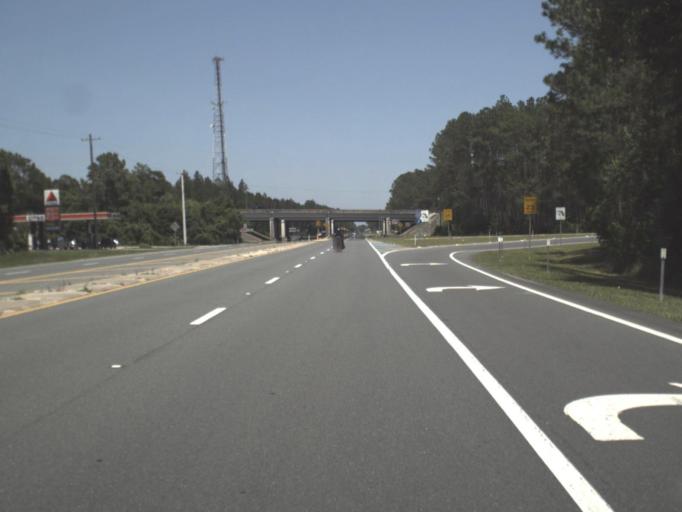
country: US
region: Florida
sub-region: Baker County
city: Macclenny
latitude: 30.2378
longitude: -82.3066
